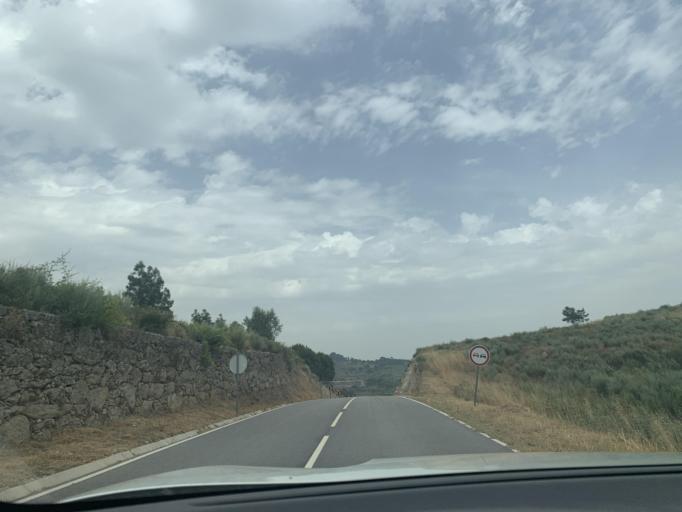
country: PT
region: Viseu
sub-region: Mangualde
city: Mangualde
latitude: 40.5692
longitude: -7.6637
